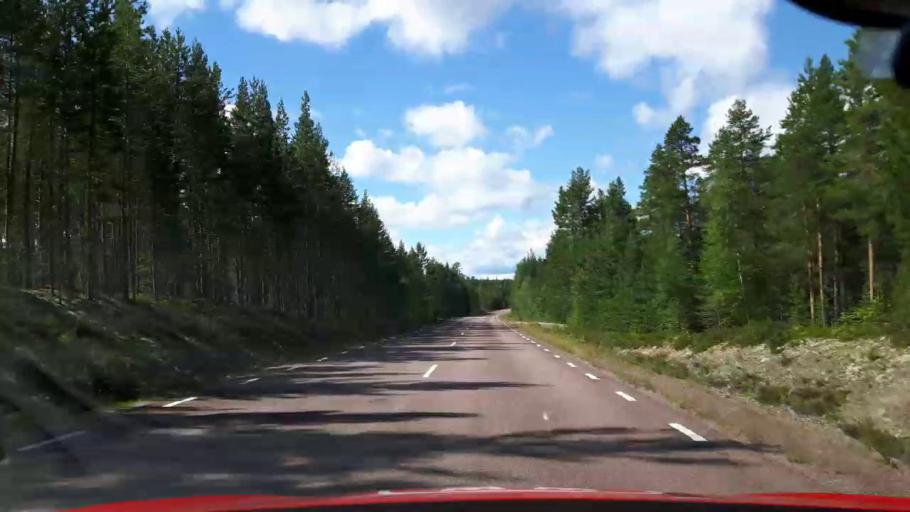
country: SE
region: Jaemtland
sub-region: Harjedalens Kommun
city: Sveg
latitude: 61.9995
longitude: 14.2633
